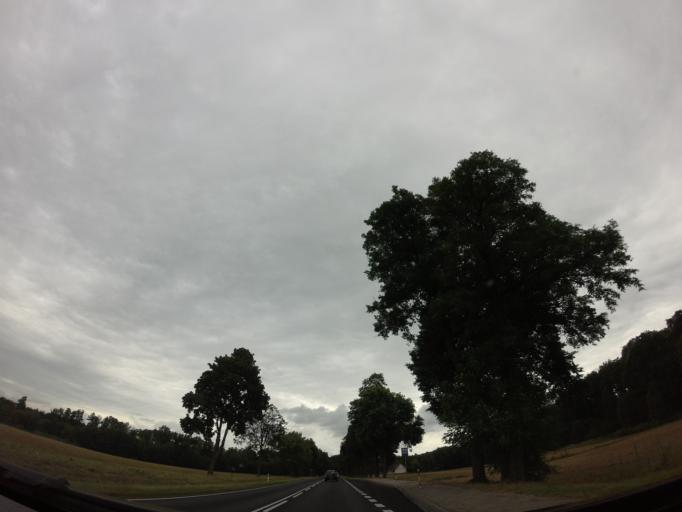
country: PL
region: Masovian Voivodeship
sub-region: Powiat ciechanowski
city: Ciechanow
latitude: 52.8571
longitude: 20.5495
